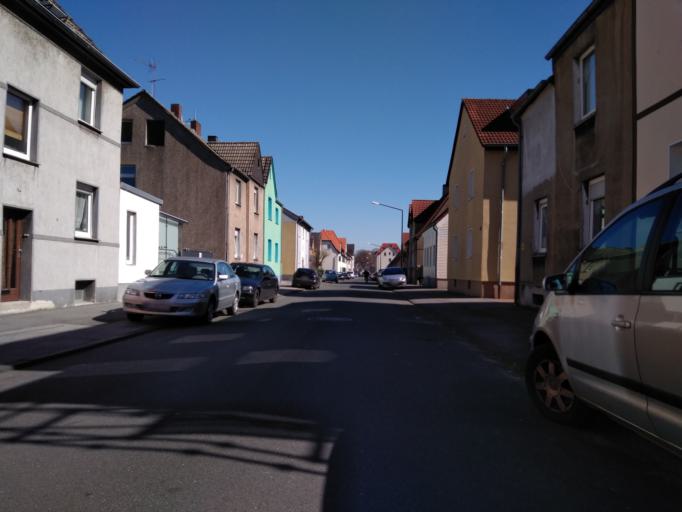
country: DE
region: North Rhine-Westphalia
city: Marl
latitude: 51.6039
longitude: 7.0815
